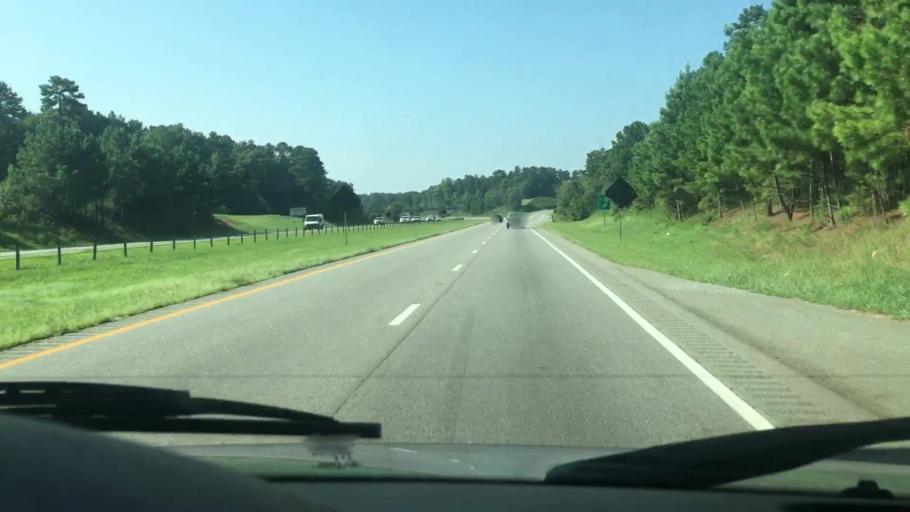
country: US
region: North Carolina
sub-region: Lincoln County
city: Lowesville
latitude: 35.3883
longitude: -80.9999
